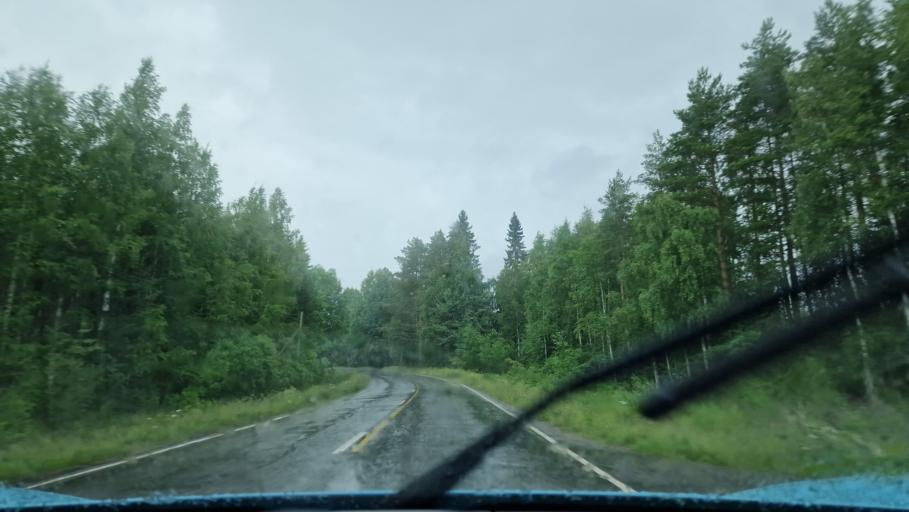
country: FI
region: Southern Ostrobothnia
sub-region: Jaerviseutu
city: Soini
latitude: 62.8273
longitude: 24.3416
